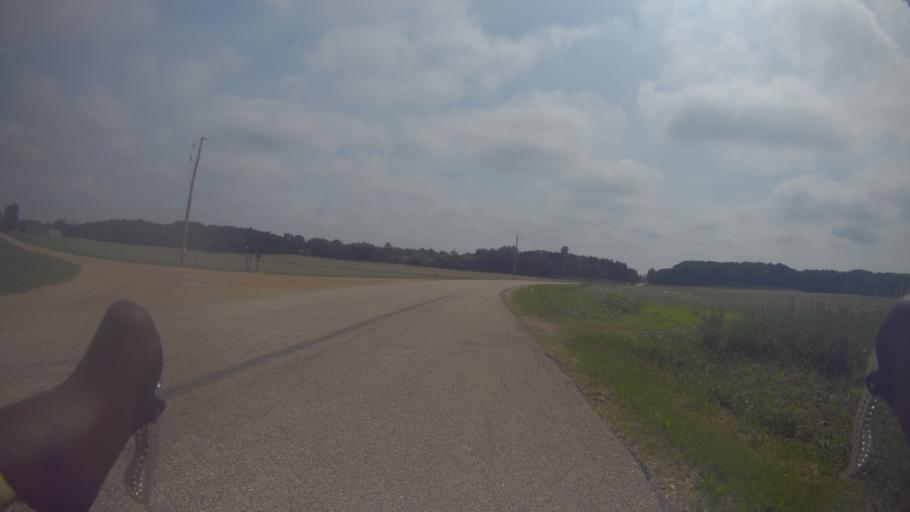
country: US
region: Wisconsin
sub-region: Jefferson County
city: Cambridge
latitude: 42.9237
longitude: -89.0145
